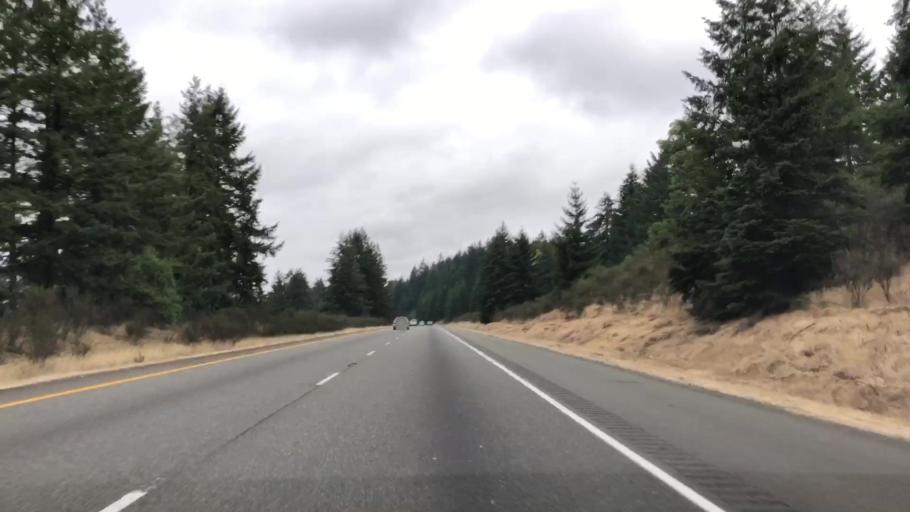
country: US
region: Washington
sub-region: Kitsap County
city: Burley
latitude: 47.4493
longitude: -122.6216
